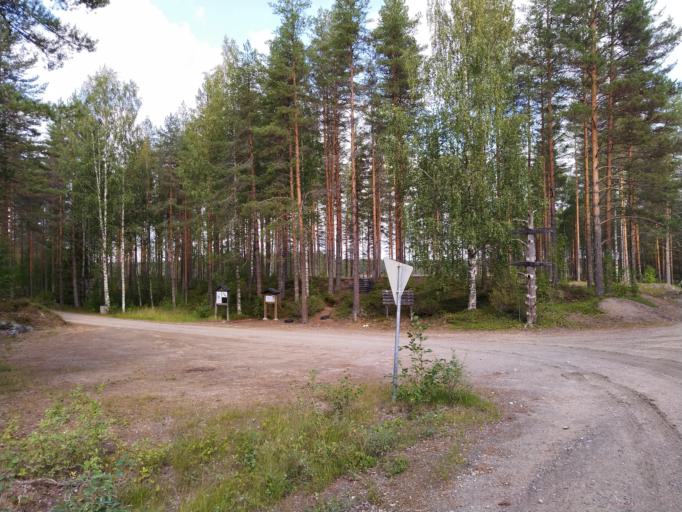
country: FI
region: North Karelia
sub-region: Pielisen Karjala
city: Lieksa
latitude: 63.5687
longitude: 30.0977
